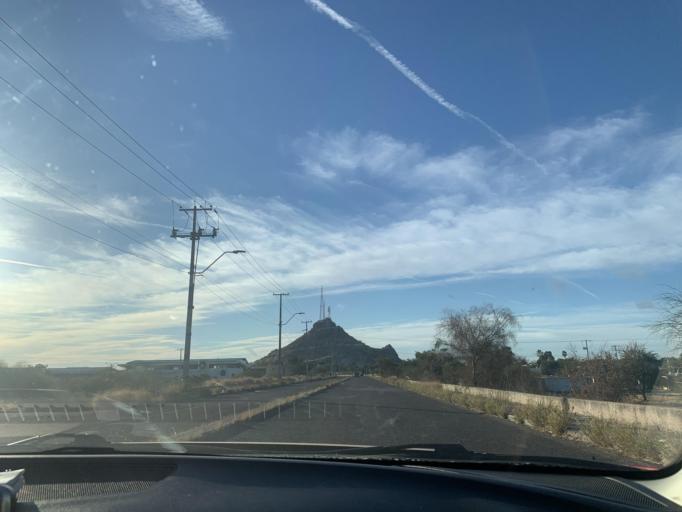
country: MX
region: Sonora
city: Hermosillo
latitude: 29.0722
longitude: -110.9348
